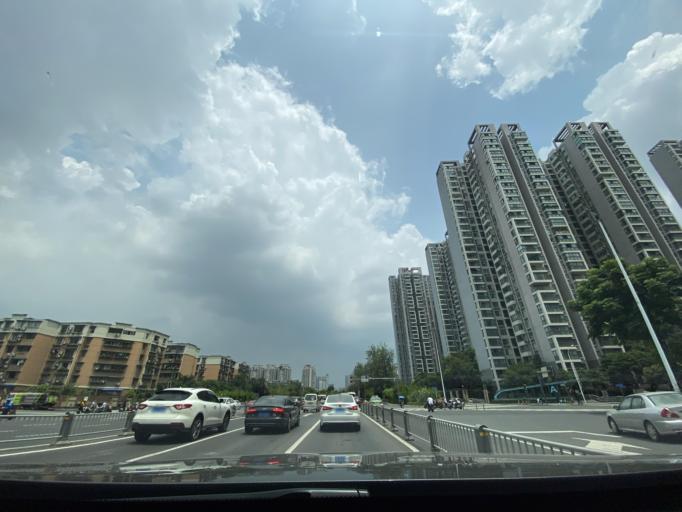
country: CN
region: Sichuan
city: Chengdu
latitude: 30.6063
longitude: 104.0751
